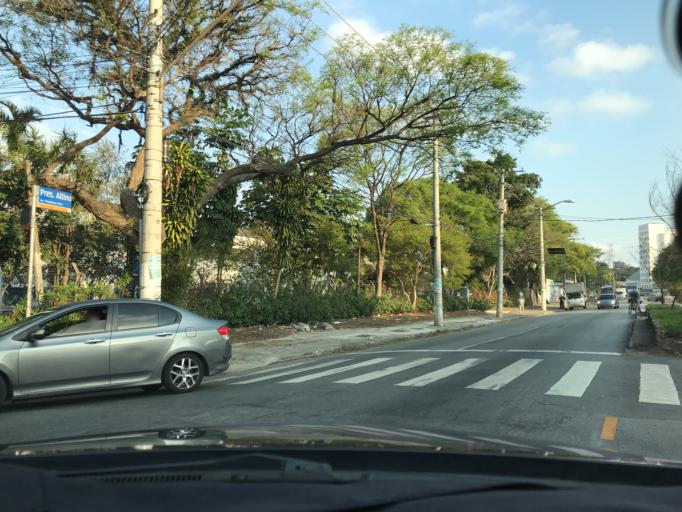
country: BR
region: Sao Paulo
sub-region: Osasco
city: Osasco
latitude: -23.5334
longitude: -46.7551
